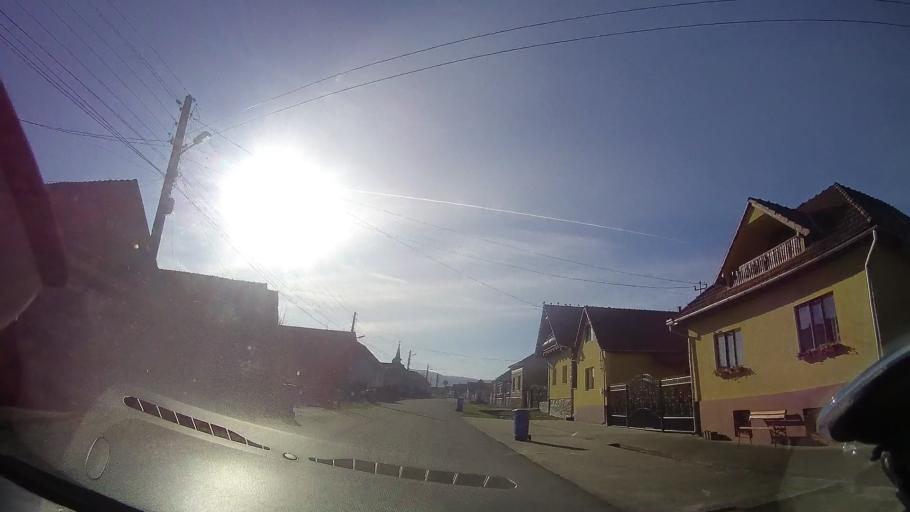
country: RO
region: Bihor
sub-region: Comuna Auseu
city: Grosi
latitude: 47.0249
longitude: 22.4731
